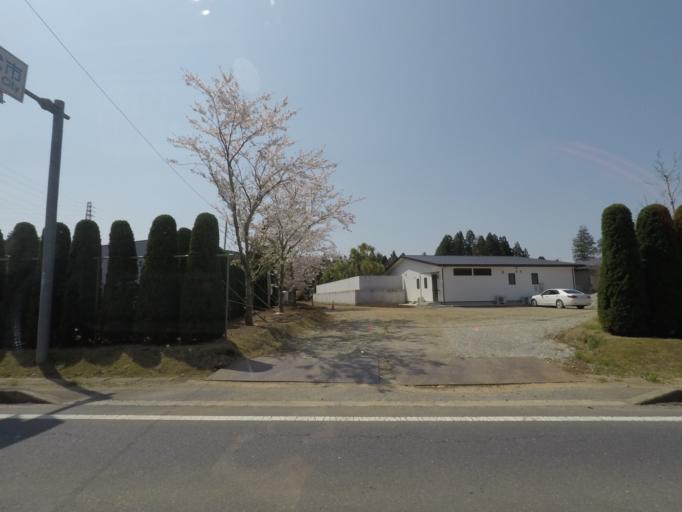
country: JP
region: Chiba
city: Naruto
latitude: 35.6805
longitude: 140.4238
